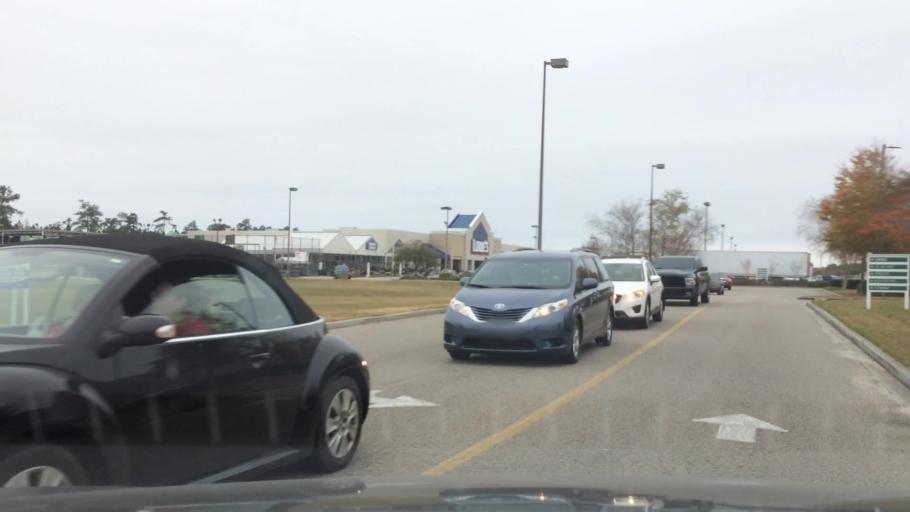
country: US
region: South Carolina
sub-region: Horry County
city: Socastee
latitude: 33.6443
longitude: -78.9874
